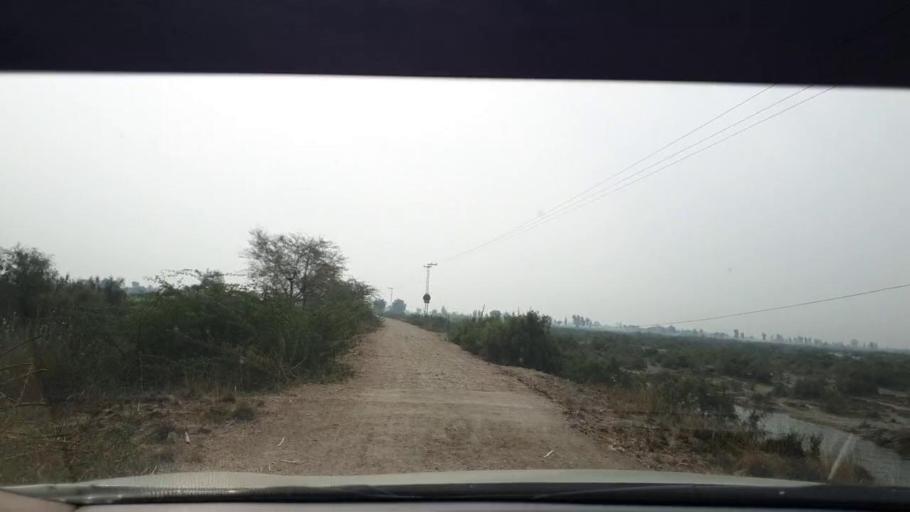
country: PK
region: Sindh
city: Berani
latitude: 25.8378
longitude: 68.8272
